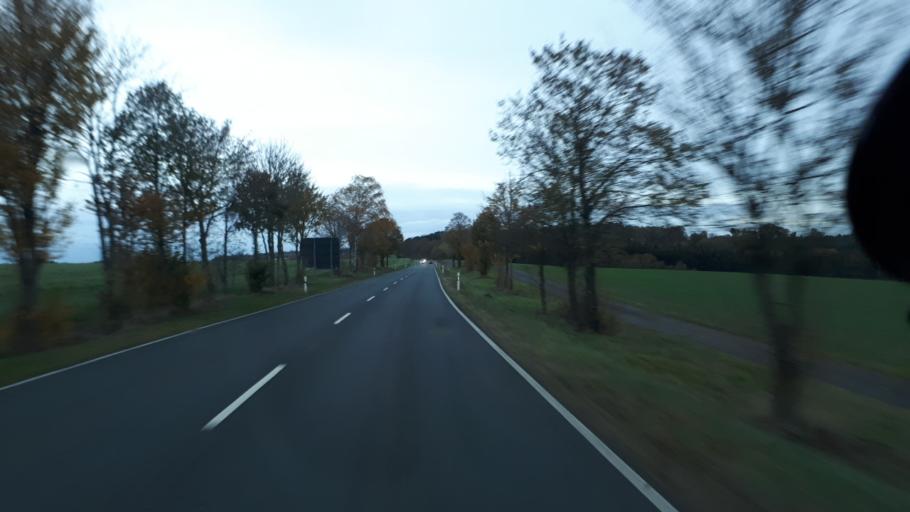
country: DE
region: Rheinland-Pfalz
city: Alflen
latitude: 50.1847
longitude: 7.0521
